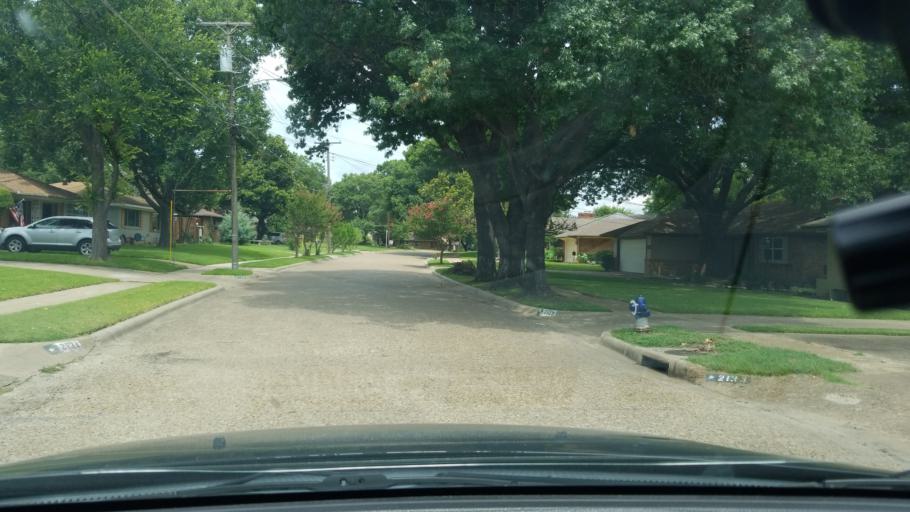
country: US
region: Texas
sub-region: Dallas County
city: Mesquite
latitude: 32.8229
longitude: -96.6790
